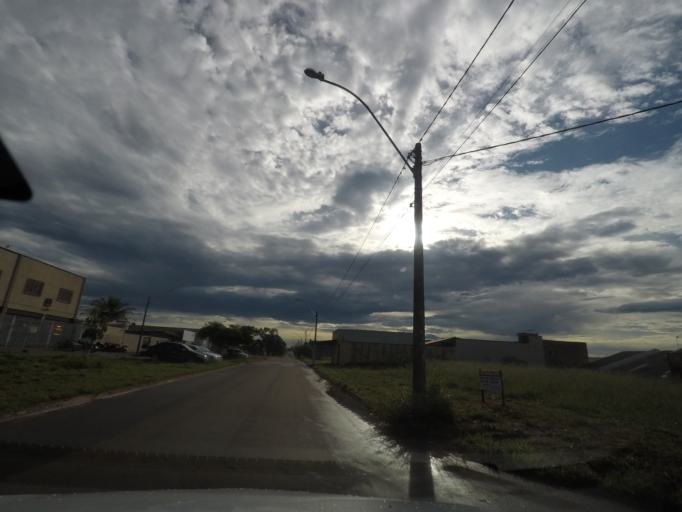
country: BR
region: Goias
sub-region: Aparecida De Goiania
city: Aparecida de Goiania
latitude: -16.7625
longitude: -49.3623
